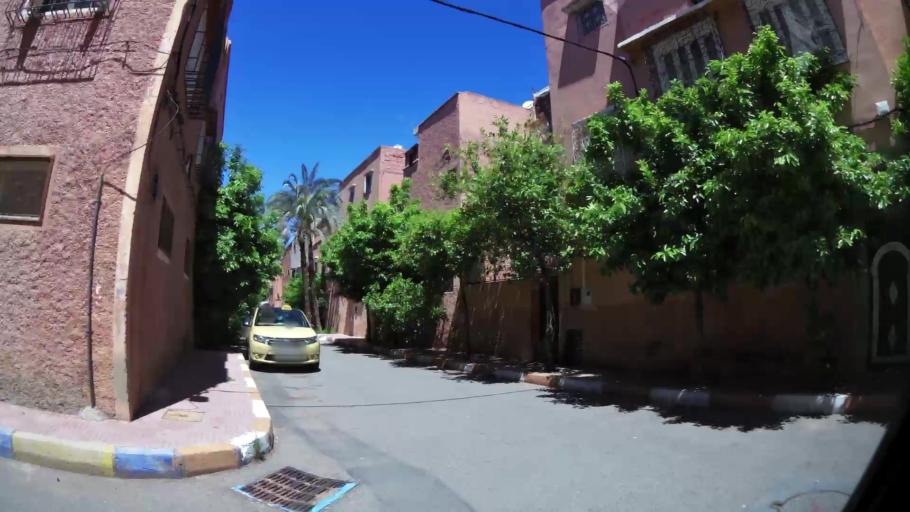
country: MA
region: Marrakech-Tensift-Al Haouz
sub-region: Marrakech
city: Marrakesh
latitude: 31.6509
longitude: -7.9998
